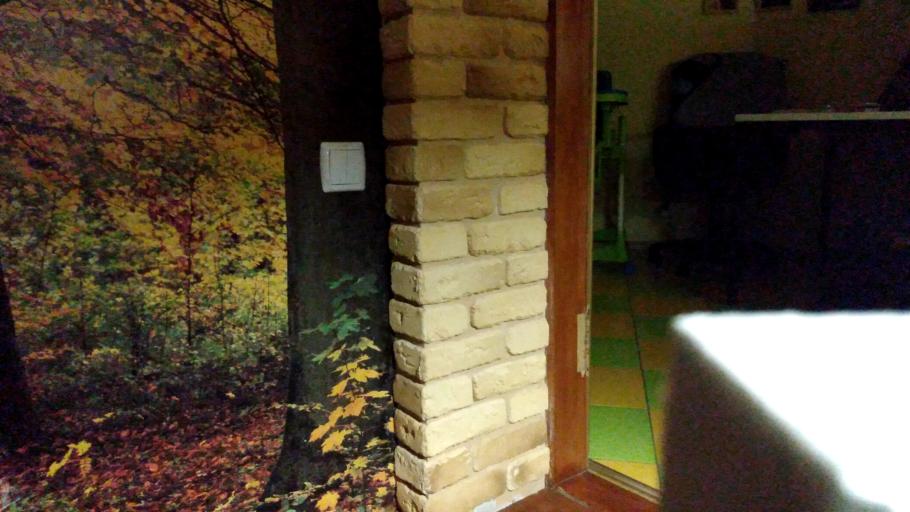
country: RU
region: Vologda
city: Lipin Bor
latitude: 60.9828
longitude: 37.9670
